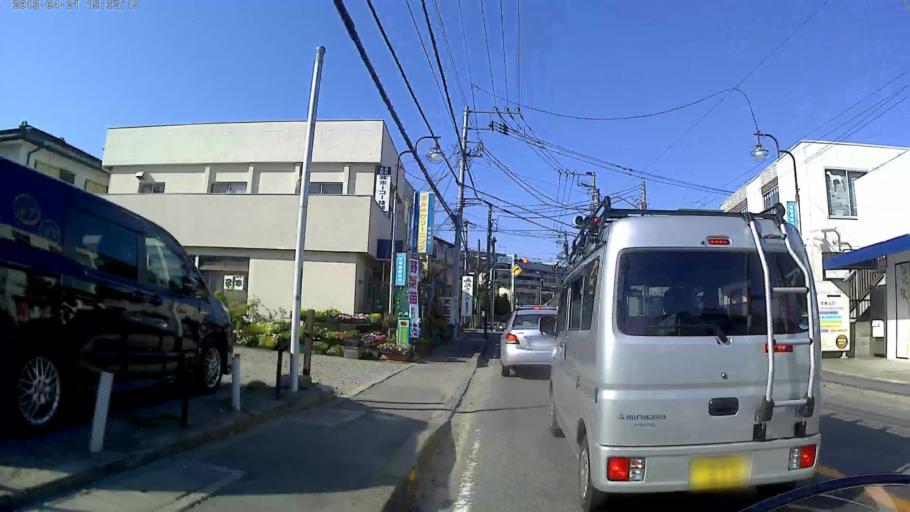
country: JP
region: Kanagawa
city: Fujisawa
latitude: 35.3179
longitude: 139.5033
